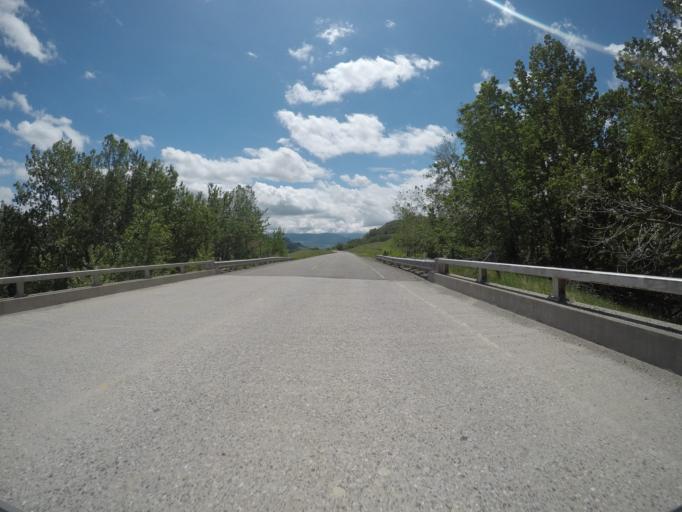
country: US
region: Montana
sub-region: Sweet Grass County
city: Big Timber
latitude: 45.6609
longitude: -110.1135
